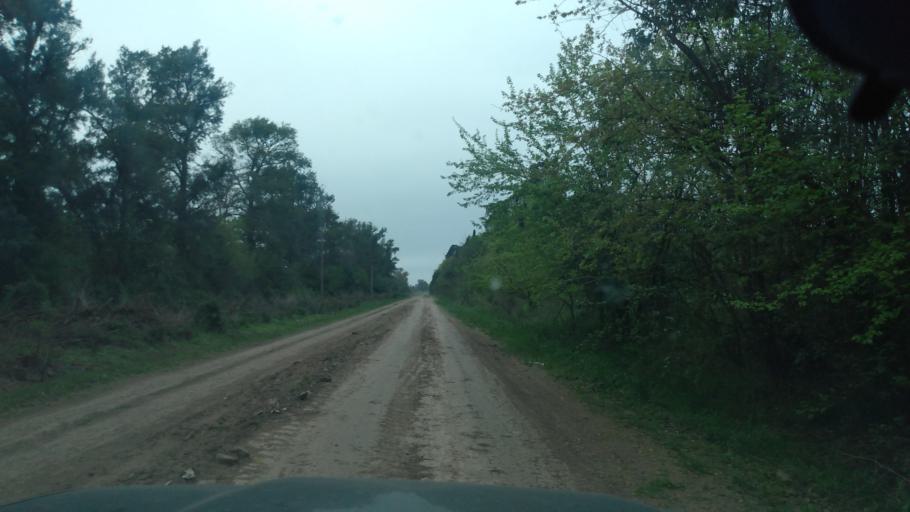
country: AR
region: Buenos Aires
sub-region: Partido de Lujan
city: Lujan
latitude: -34.5413
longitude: -59.2046
